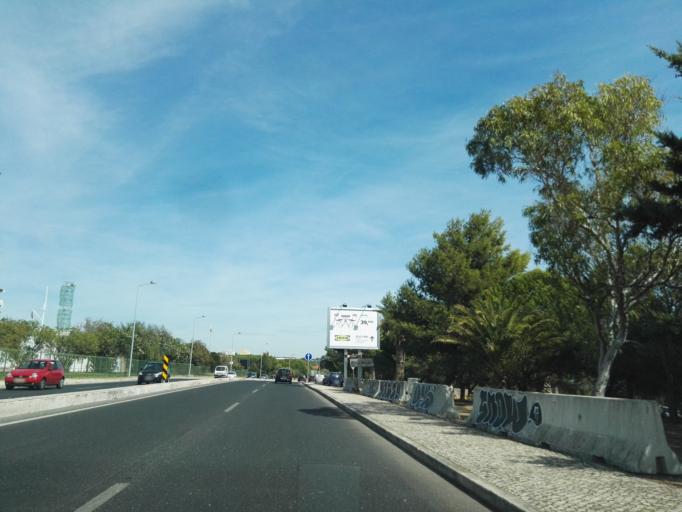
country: PT
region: Lisbon
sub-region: Oeiras
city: Paco de Arcos
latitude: 38.6898
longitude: -9.2997
